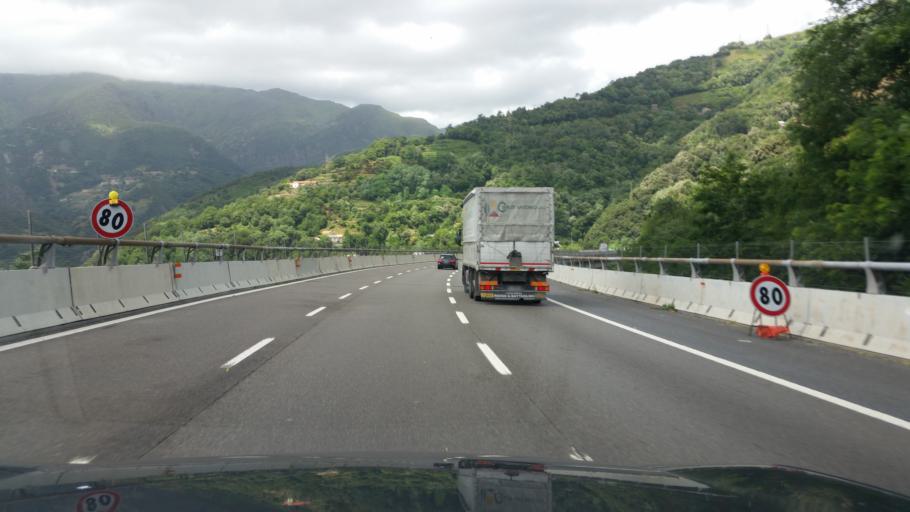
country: IT
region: Liguria
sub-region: Provincia di Genova
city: Mele
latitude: 44.4479
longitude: 8.7313
